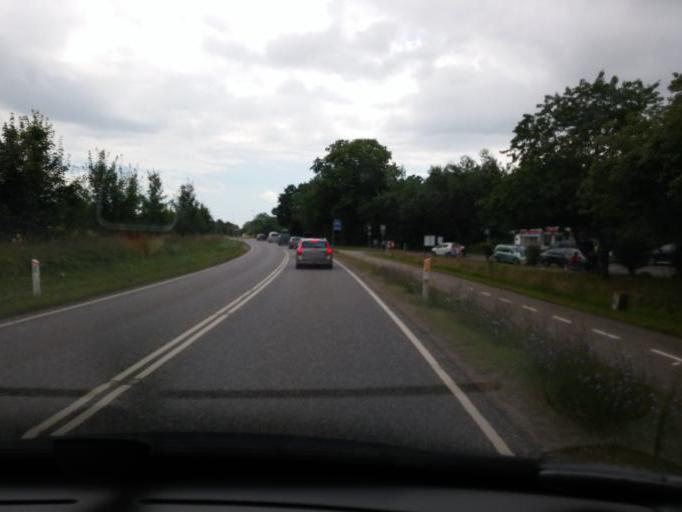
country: DK
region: South Denmark
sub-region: Svendborg Kommune
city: Vindeby
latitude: 55.0000
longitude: 10.6082
